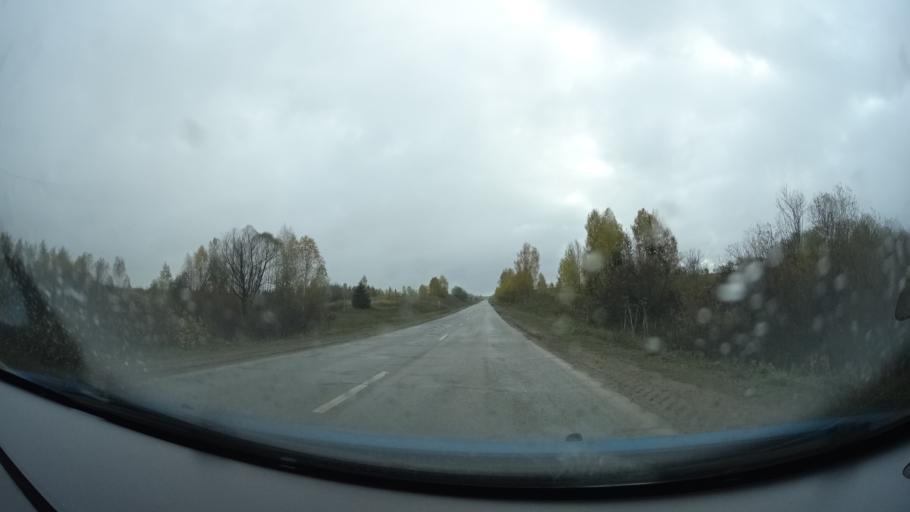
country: RU
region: Perm
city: Chernushka
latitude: 56.7517
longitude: 56.1510
